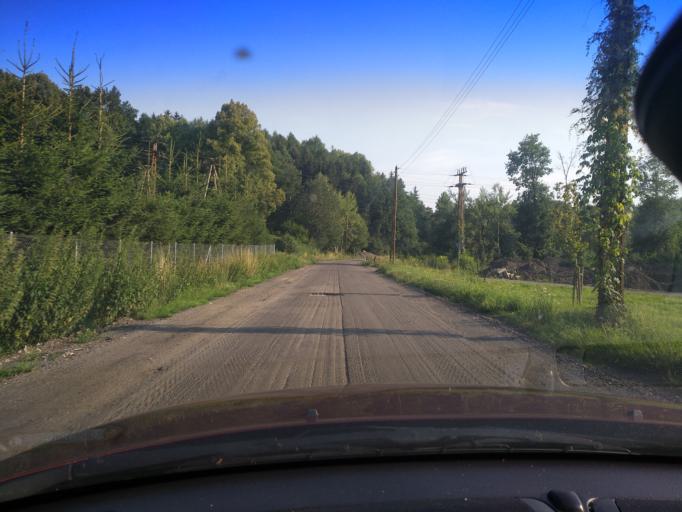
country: PL
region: Lower Silesian Voivodeship
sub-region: Powiat lubanski
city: Lesna
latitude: 51.0195
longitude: 15.2752
